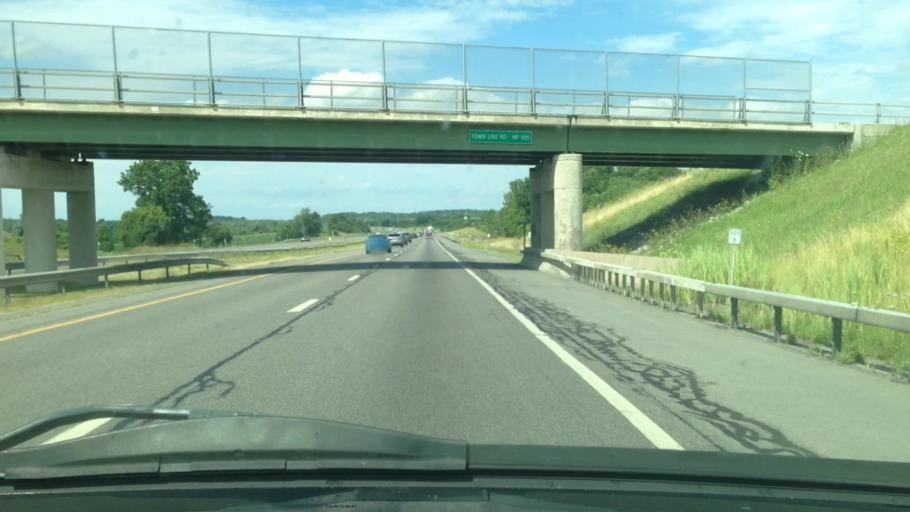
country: US
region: New York
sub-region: Cayuga County
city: Centerport
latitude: 43.0552
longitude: -76.5947
